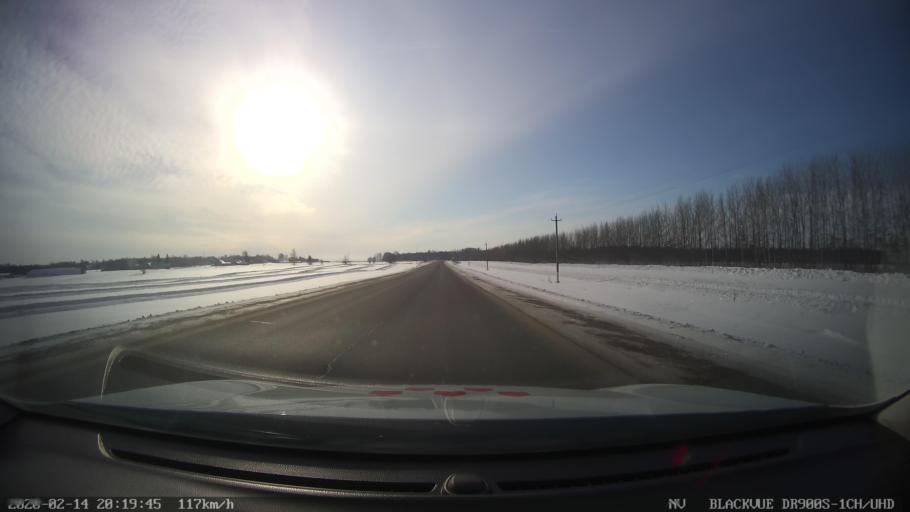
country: RU
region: Tatarstan
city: Verkhniy Uslon
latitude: 55.5662
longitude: 48.9014
